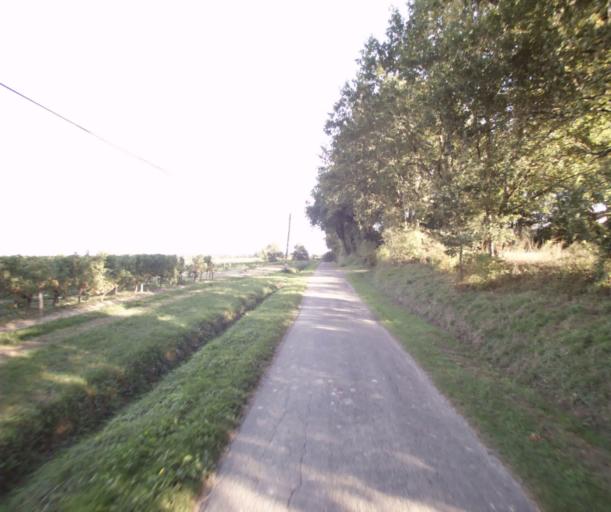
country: FR
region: Midi-Pyrenees
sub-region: Departement du Gers
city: Eauze
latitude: 43.8551
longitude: 0.0122
